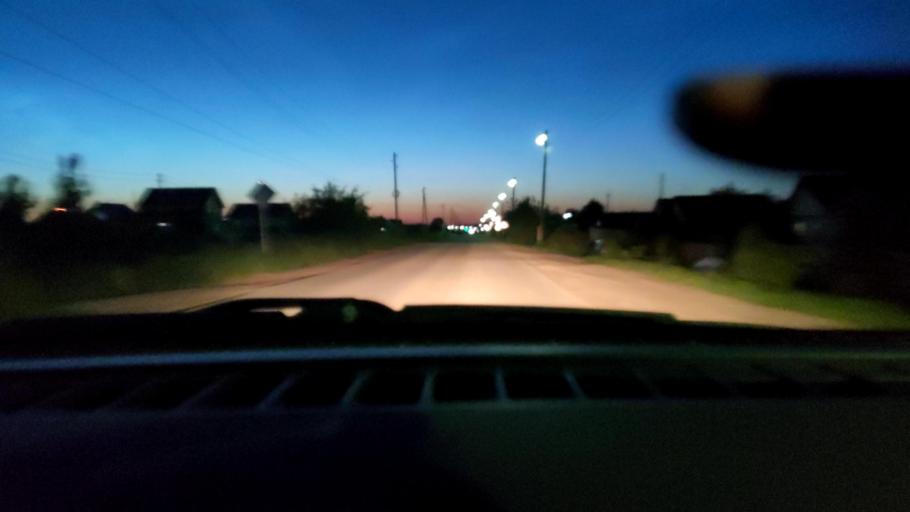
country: RU
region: Perm
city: Kultayevo
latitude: 57.8688
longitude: 55.9168
